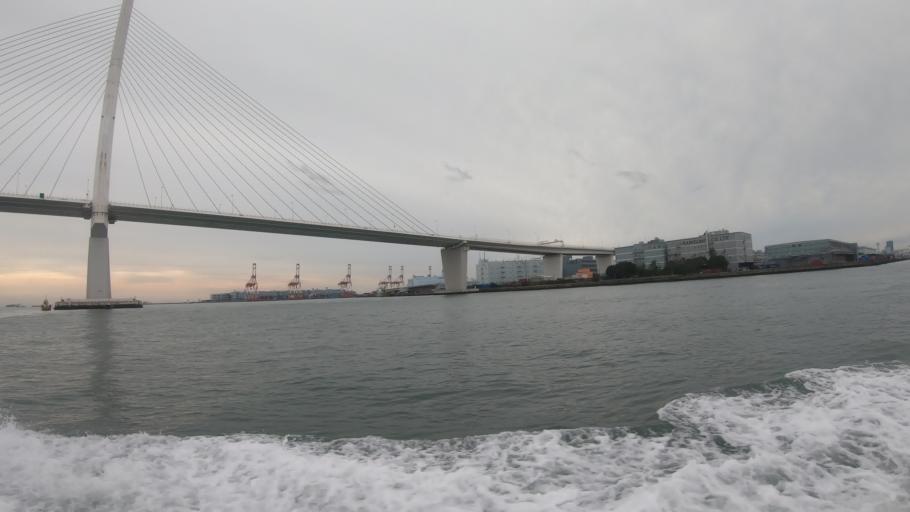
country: JP
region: Kanagawa
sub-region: Kawasaki-shi
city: Kawasaki
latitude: 35.4732
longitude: 139.6951
